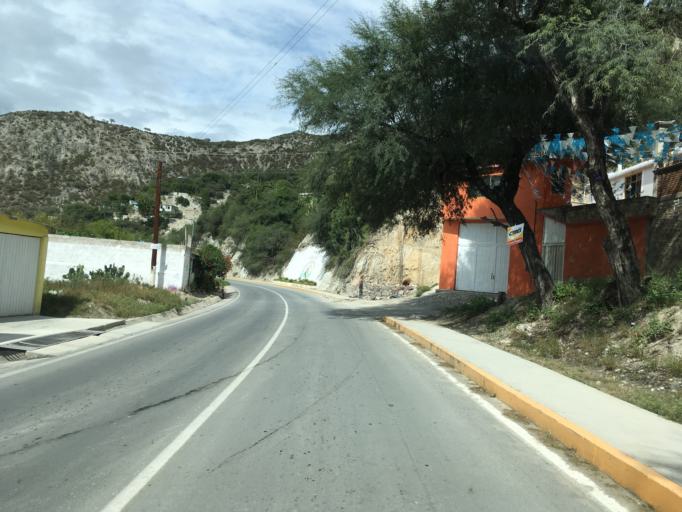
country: MX
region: Hidalgo
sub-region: San Agustin Metzquititlan
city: Mezquititlan
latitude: 20.5008
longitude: -98.6954
